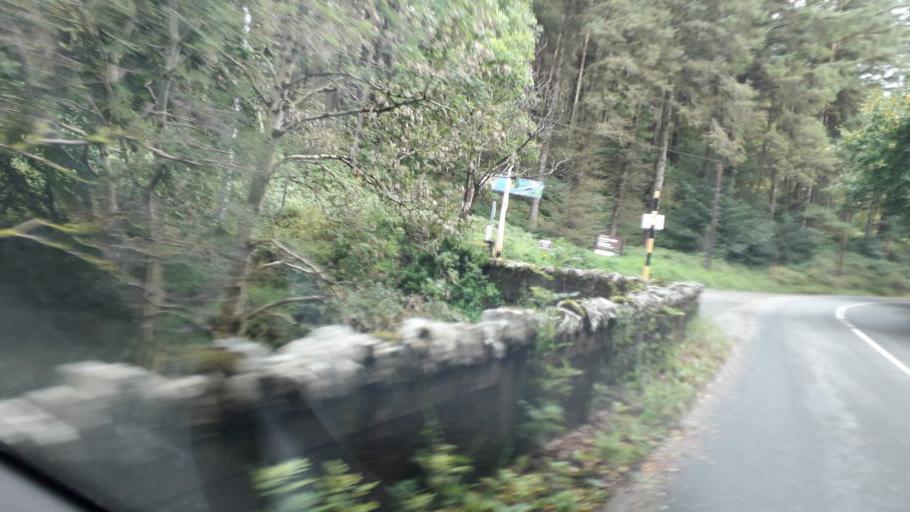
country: IE
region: Leinster
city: Ballyboden
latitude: 53.2428
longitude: -6.2952
